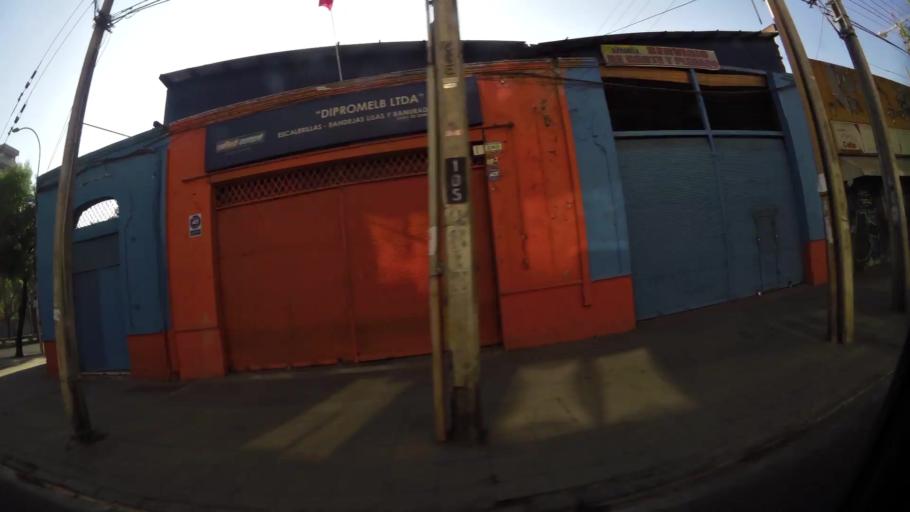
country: CL
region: Santiago Metropolitan
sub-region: Provincia de Santiago
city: Santiago
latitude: -33.4595
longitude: -70.6472
